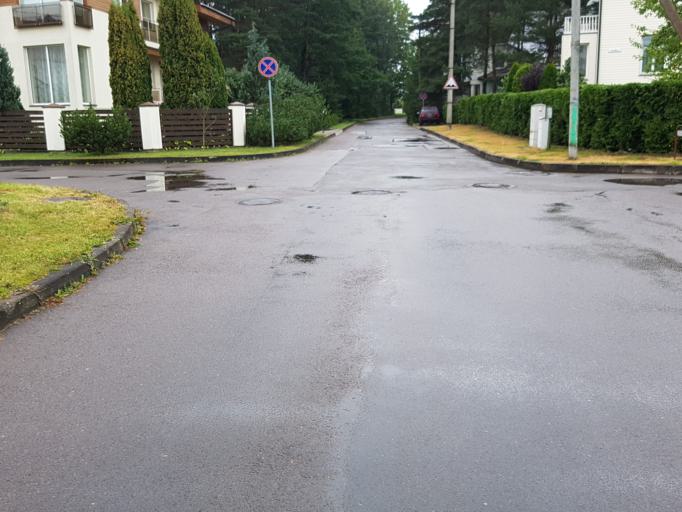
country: LT
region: Vilnius County
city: Lazdynai
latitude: 54.6607
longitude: 25.1853
